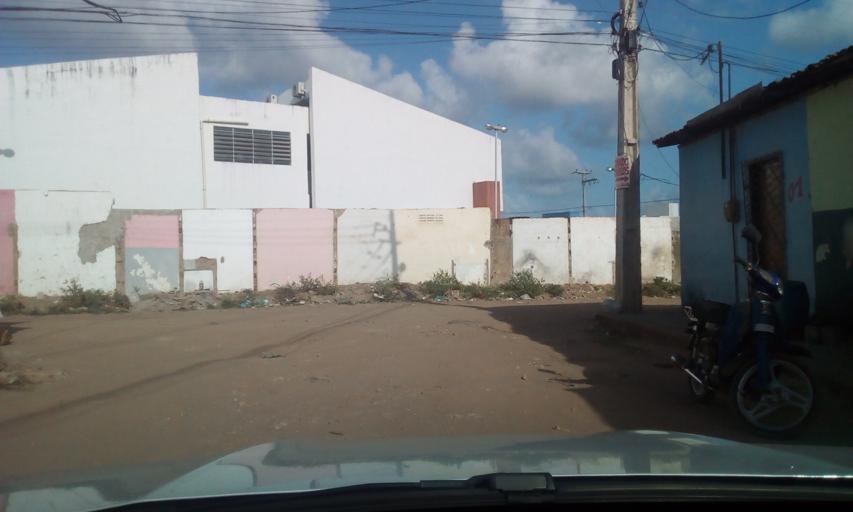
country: BR
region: Paraiba
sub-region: Joao Pessoa
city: Joao Pessoa
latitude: -7.1862
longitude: -34.8814
